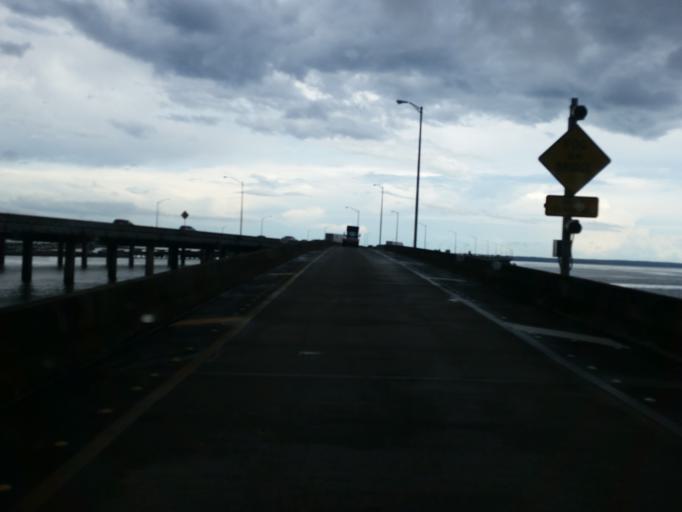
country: US
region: Alabama
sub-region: Mobile County
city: Mobile
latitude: 30.6772
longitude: -87.9877
